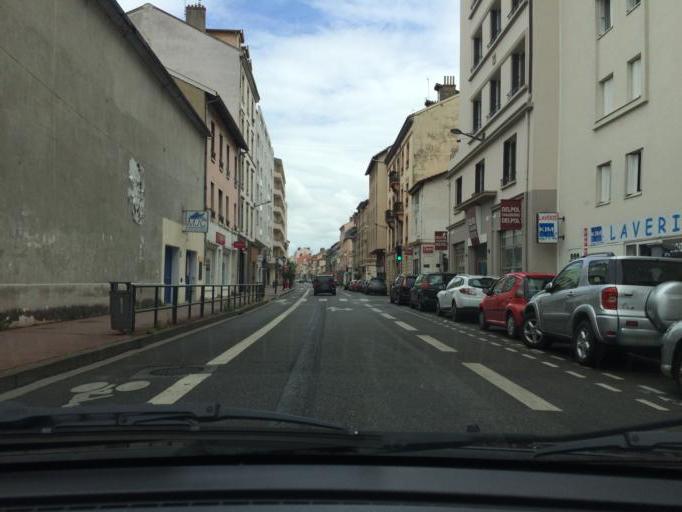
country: FR
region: Rhone-Alpes
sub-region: Departement du Rhone
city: Lyon
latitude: 45.7460
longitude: 4.8631
